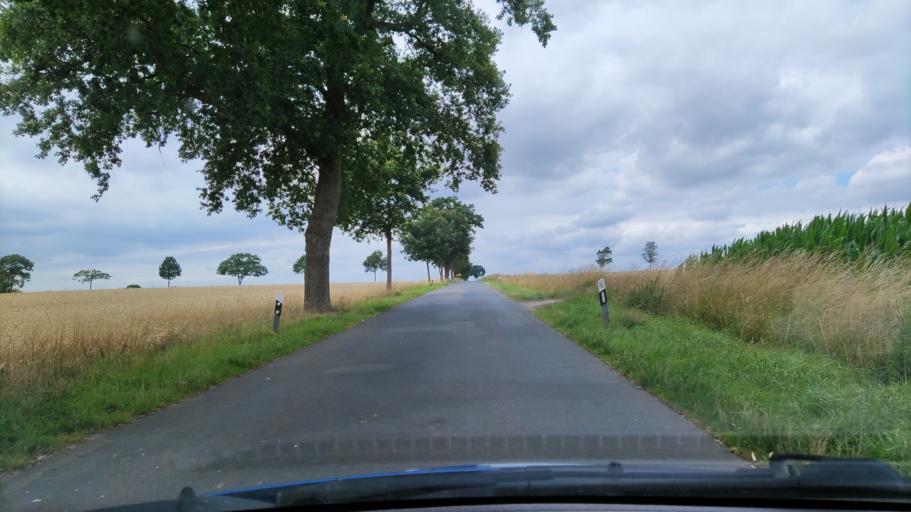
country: DE
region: Lower Saxony
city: Romstedt
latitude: 53.0849
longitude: 10.6754
